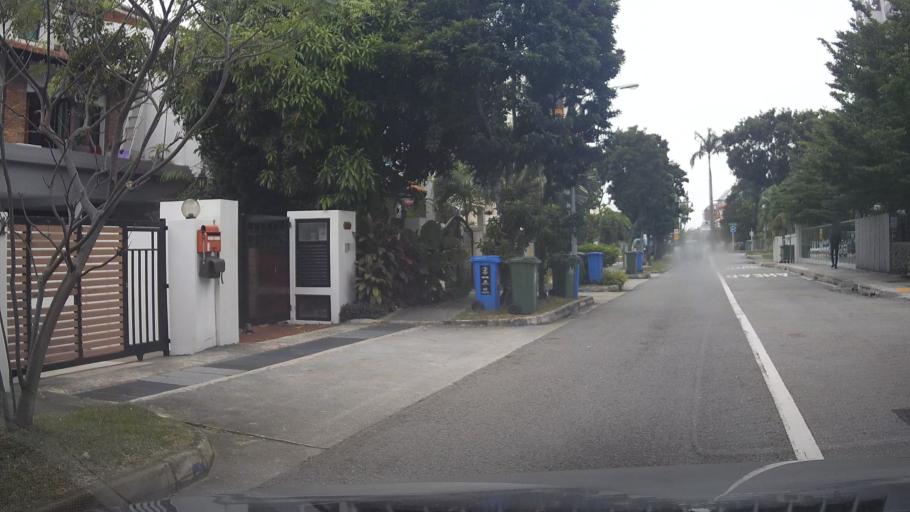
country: SG
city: Singapore
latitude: 1.3152
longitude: 103.9050
